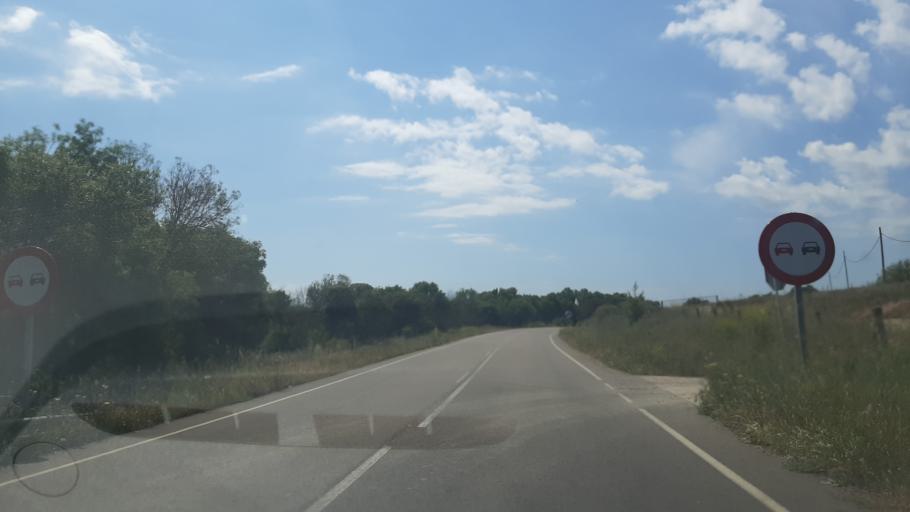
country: ES
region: Castille and Leon
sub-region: Provincia de Salamanca
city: Gallegos de Arganan
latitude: 40.6062
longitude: -6.7058
